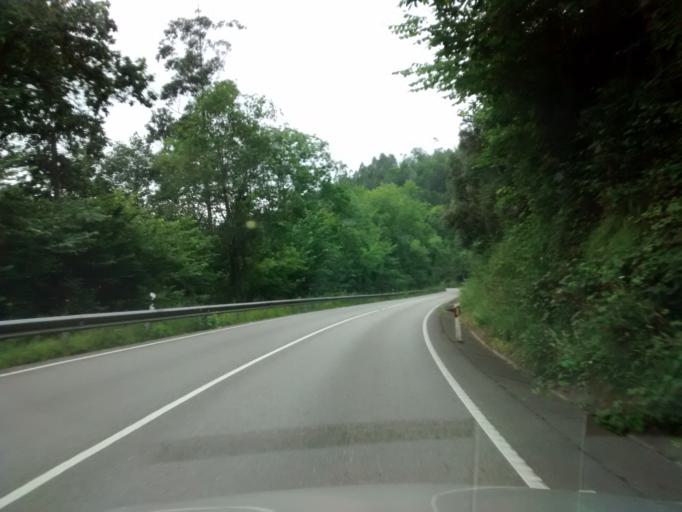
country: ES
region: Asturias
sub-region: Province of Asturias
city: Villaviciosa
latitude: 43.4431
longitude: -5.4387
